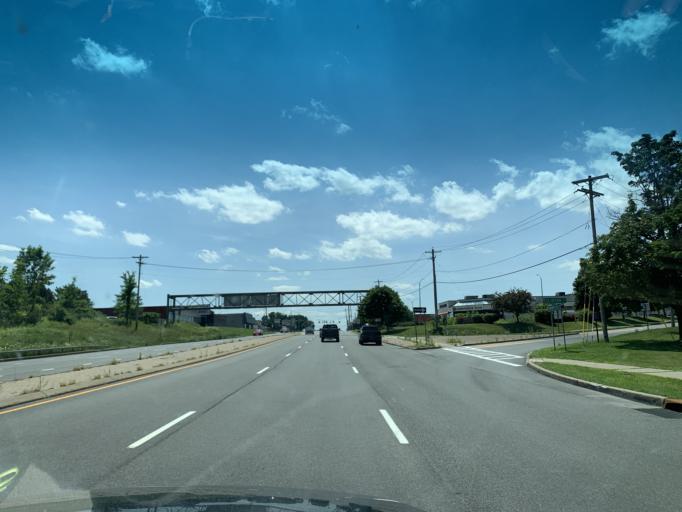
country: US
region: New York
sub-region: Oneida County
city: New York Mills
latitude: 43.0906
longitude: -75.3100
